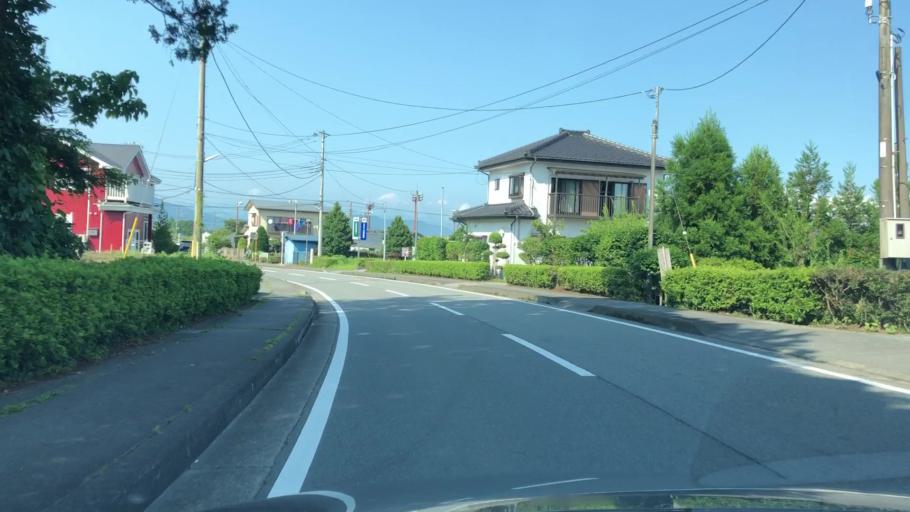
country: JP
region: Shizuoka
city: Gotemba
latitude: 35.3118
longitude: 138.9081
